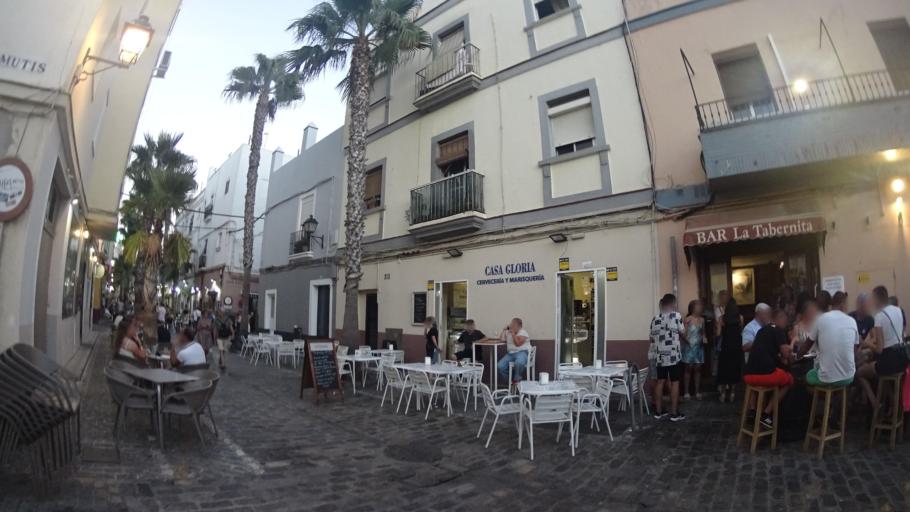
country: ES
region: Andalusia
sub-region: Provincia de Cadiz
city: Cadiz
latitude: 36.5298
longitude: -6.3039
